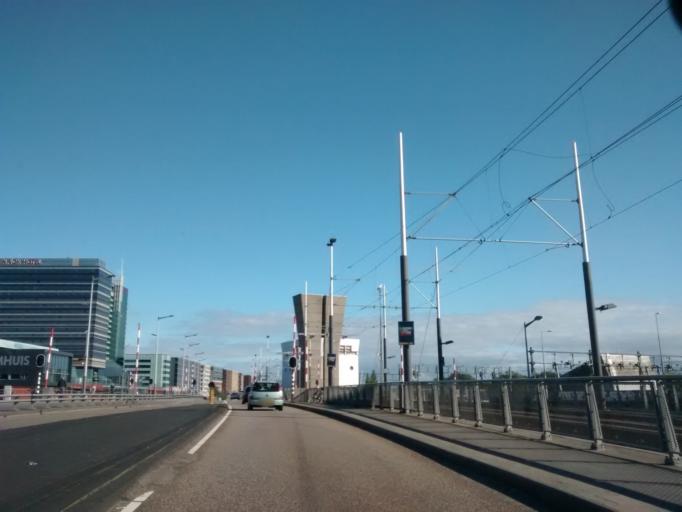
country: NL
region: North Holland
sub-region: Gemeente Amsterdam
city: Amsterdam
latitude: 52.3776
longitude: 4.9094
